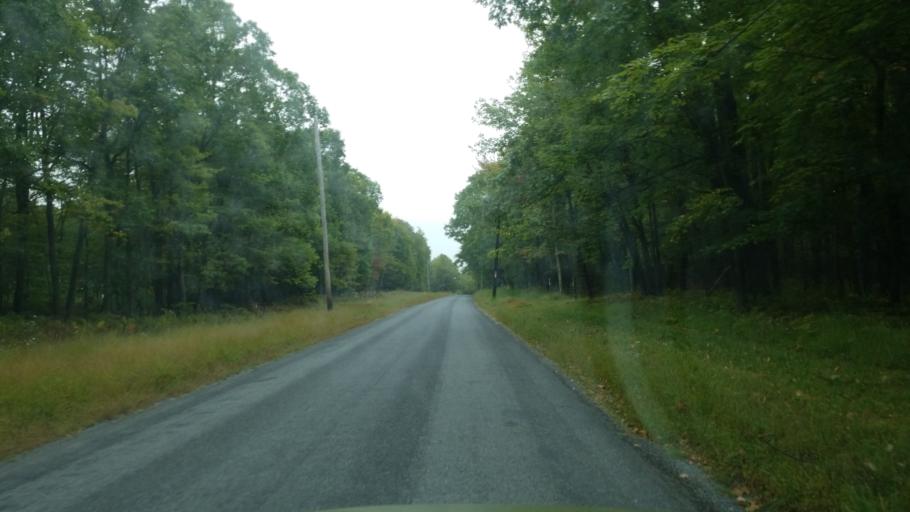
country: US
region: Pennsylvania
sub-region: Clearfield County
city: Curwensville
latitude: 41.0348
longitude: -78.5611
